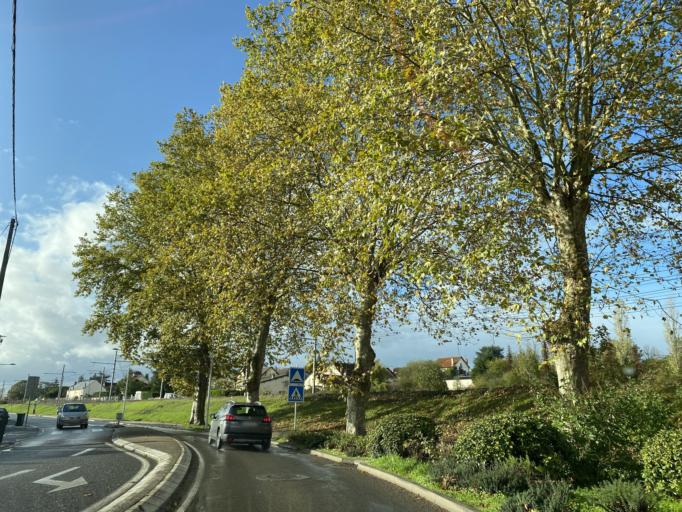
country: FR
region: Centre
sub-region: Departement du Cher
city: Bourges
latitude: 47.0949
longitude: 2.3785
